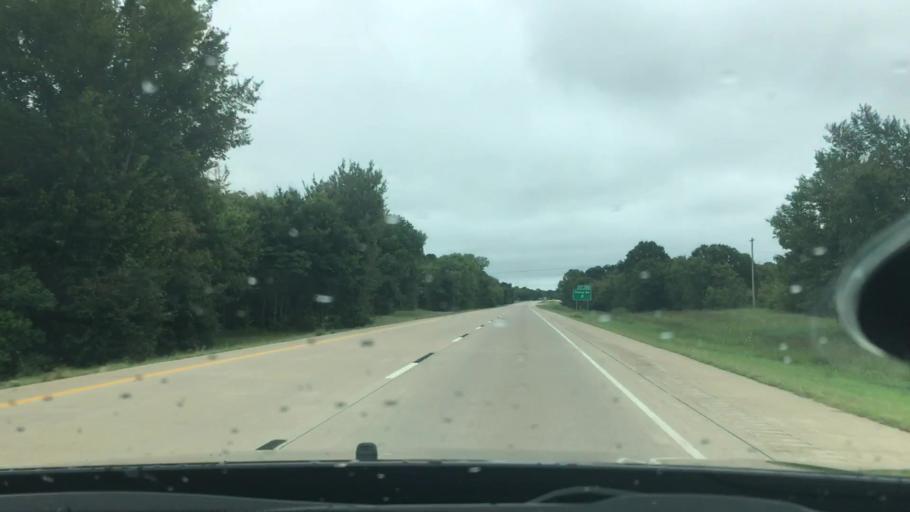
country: US
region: Oklahoma
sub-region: McIntosh County
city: Checotah
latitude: 35.4508
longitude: -95.7260
